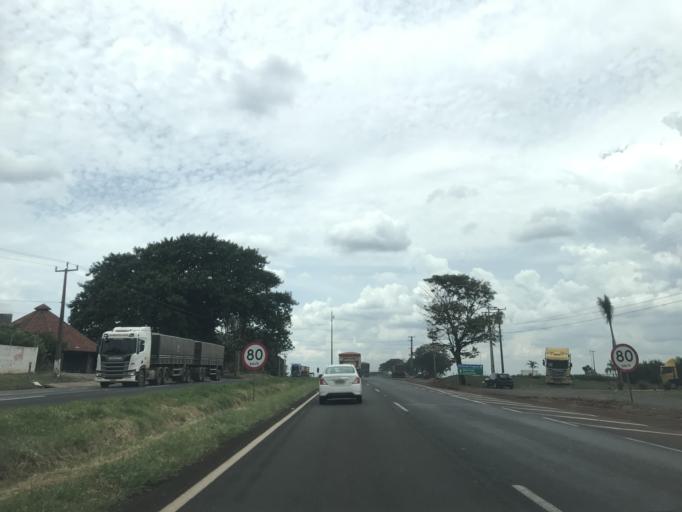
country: BR
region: Parana
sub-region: Maringa
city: Maringa
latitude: -23.3991
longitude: -52.0021
